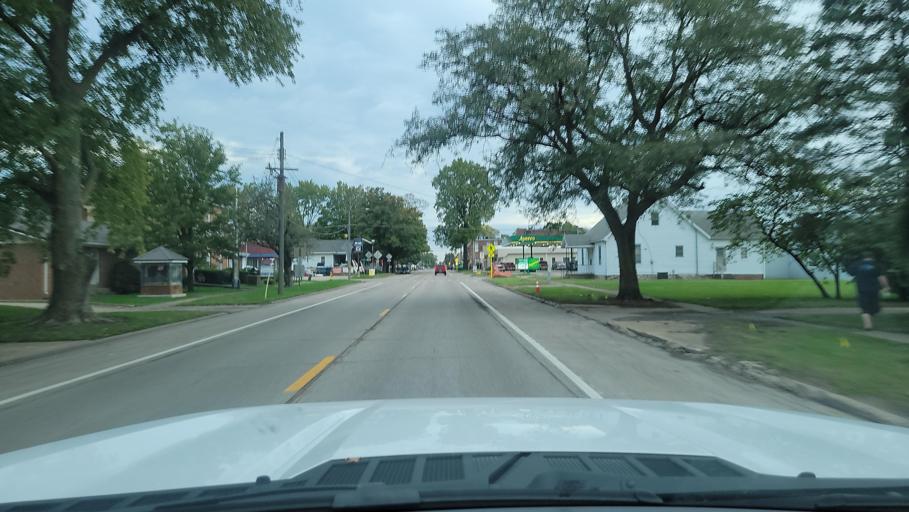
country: US
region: Illinois
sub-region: Schuyler County
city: Rushville
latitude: 40.1183
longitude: -90.5636
